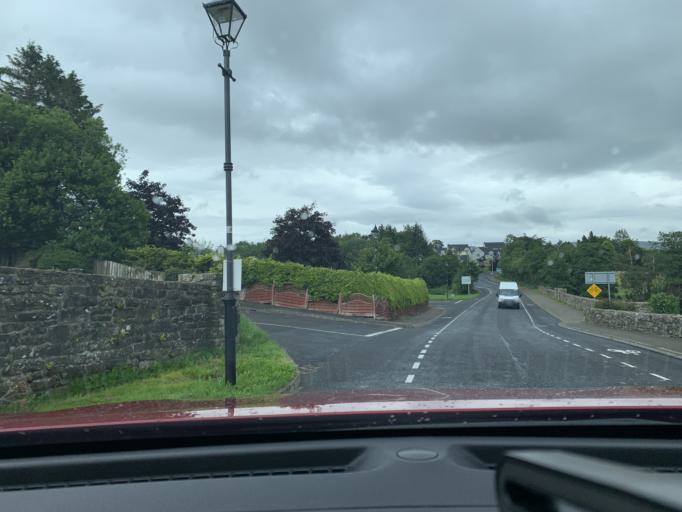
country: IE
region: Connaught
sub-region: County Leitrim
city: Manorhamilton
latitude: 54.3071
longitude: -8.1796
